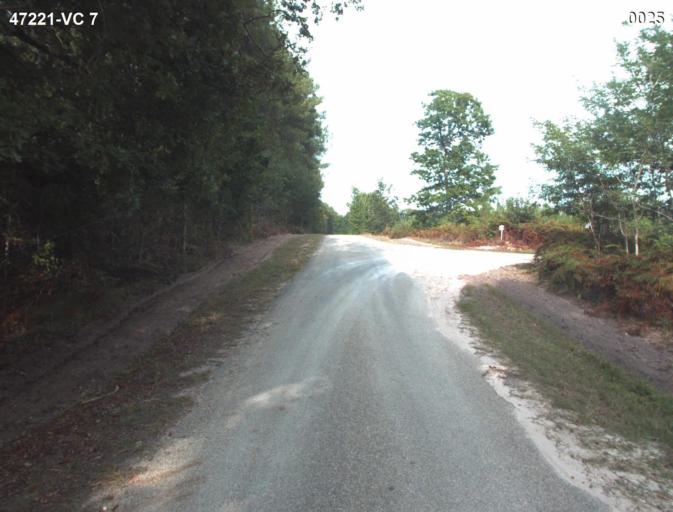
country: FR
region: Aquitaine
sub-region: Departement du Lot-et-Garonne
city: Mezin
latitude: 44.0991
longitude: 0.2271
